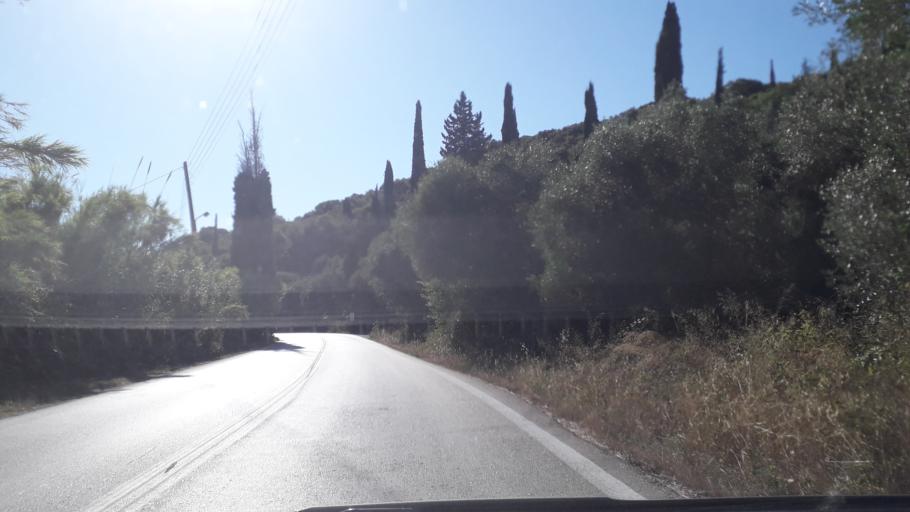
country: GR
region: Ionian Islands
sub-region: Nomos Kerkyras
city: Agios Matthaios
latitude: 39.4772
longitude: 19.9234
